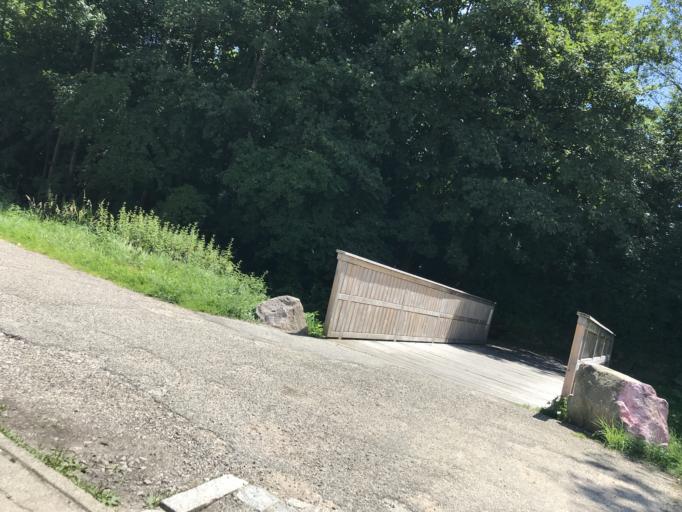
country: DE
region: Baden-Wuerttemberg
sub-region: Freiburg Region
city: Schopfheim
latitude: 47.6441
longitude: 7.8208
